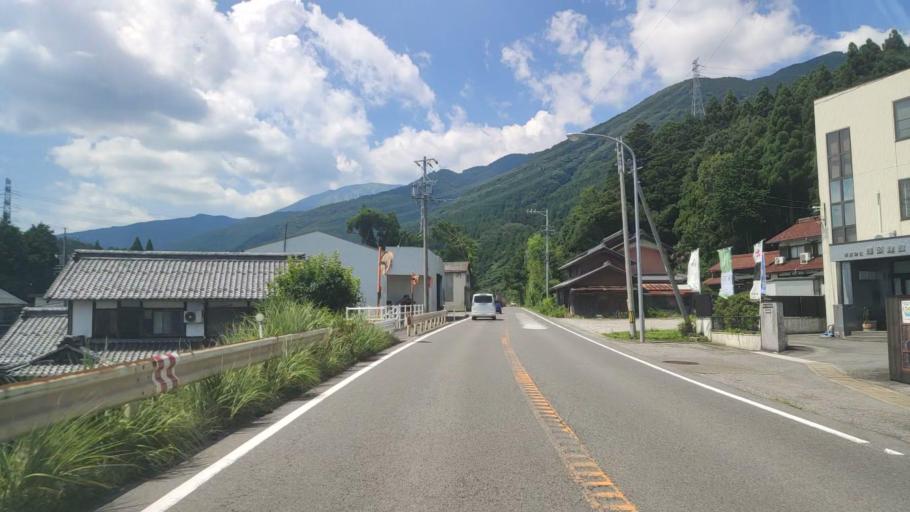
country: JP
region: Gifu
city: Tarui
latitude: 35.3733
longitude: 136.4439
